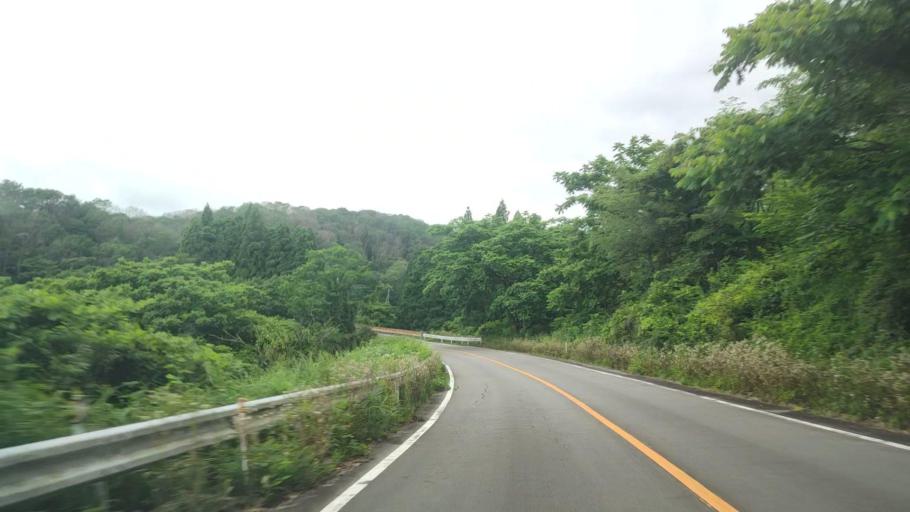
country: JP
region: Tottori
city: Kurayoshi
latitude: 35.3010
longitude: 133.6266
